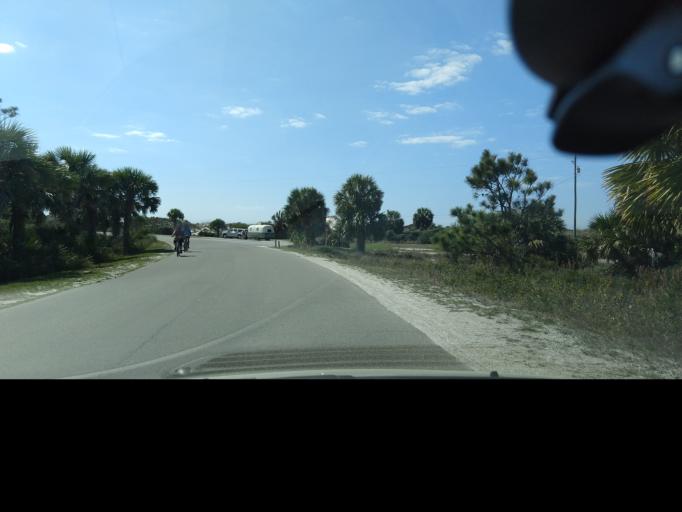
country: US
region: Florida
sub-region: Gulf County
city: Port Saint Joe
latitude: 29.7732
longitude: -85.4051
